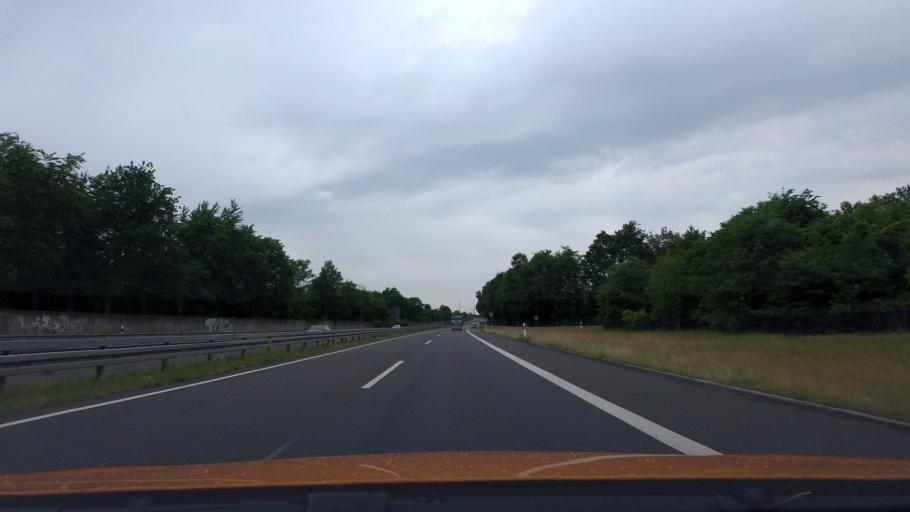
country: DE
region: Lower Saxony
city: Nienburg
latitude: 52.6486
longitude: 9.2283
